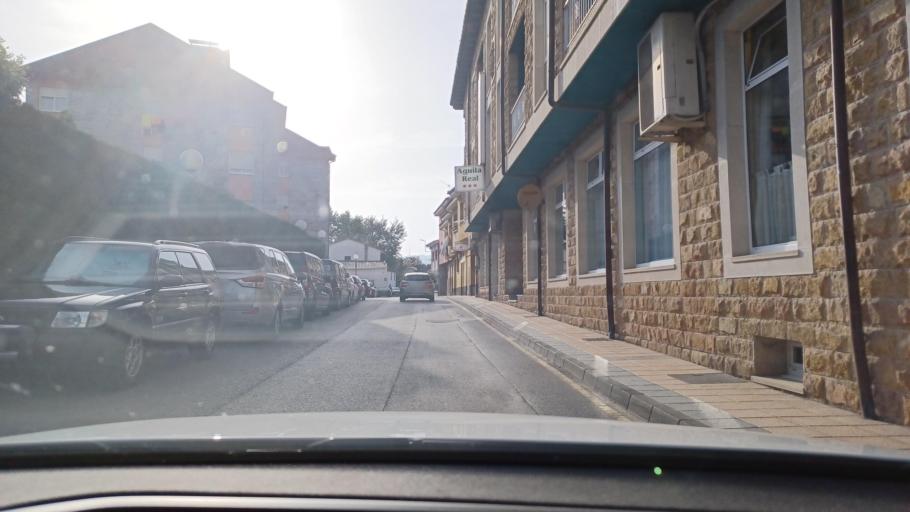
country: ES
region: Asturias
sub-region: Province of Asturias
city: Cangas de Onis
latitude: 43.3518
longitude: -5.1253
